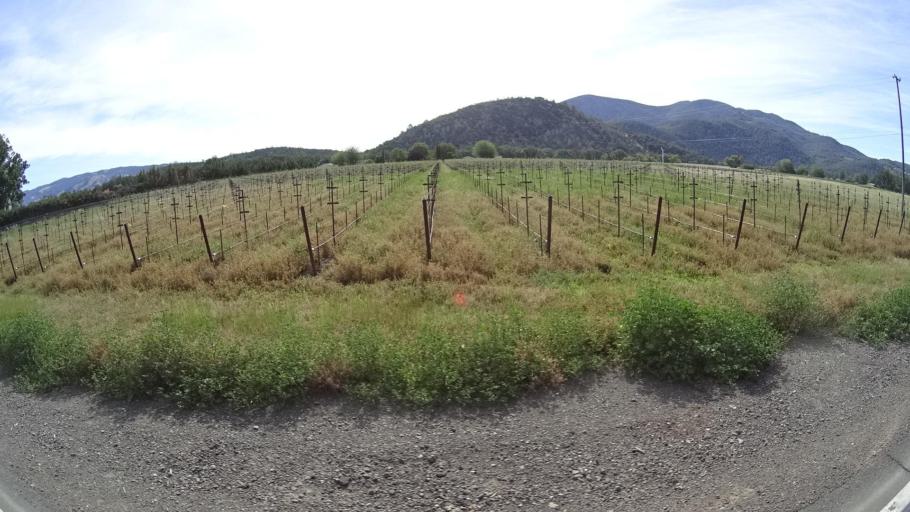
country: US
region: California
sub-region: Lake County
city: Kelseyville
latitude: 39.0060
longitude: -122.8290
